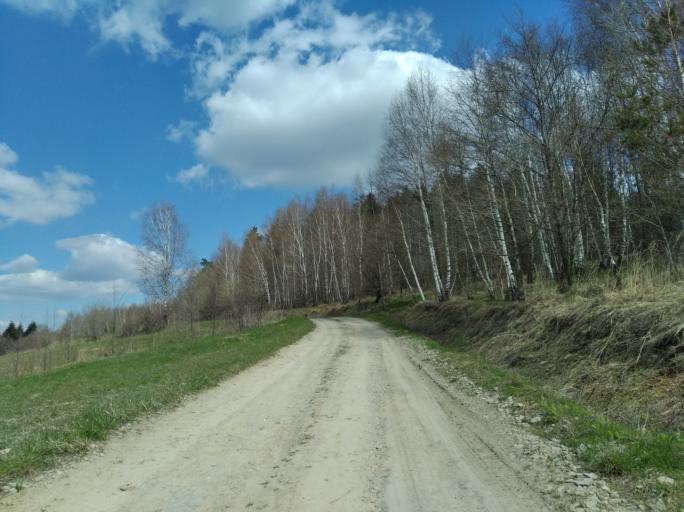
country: PL
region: Subcarpathian Voivodeship
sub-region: Powiat strzyzowski
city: Wysoka Strzyzowska
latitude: 49.8264
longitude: 21.7706
